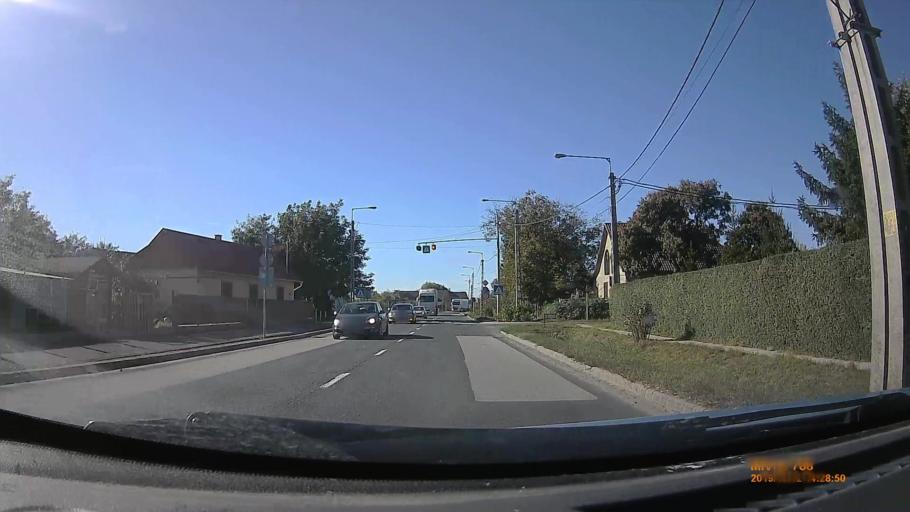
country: HU
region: Hajdu-Bihar
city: Berettyoujfalu
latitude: 47.1682
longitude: 21.6201
